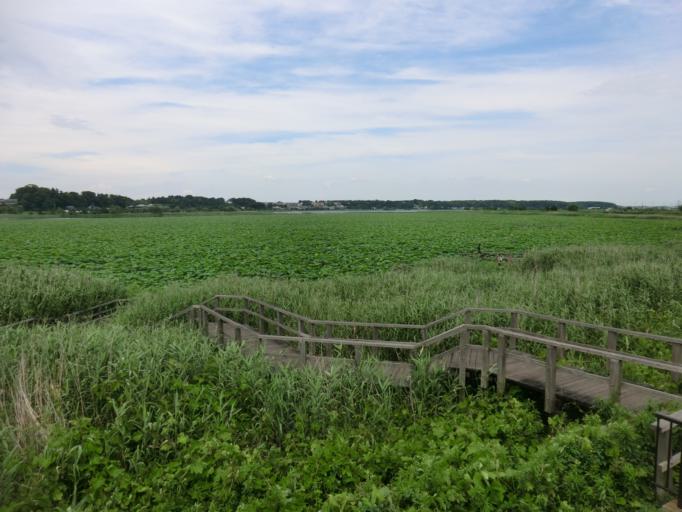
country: JP
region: Chiba
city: Abiko
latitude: 35.8539
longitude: 140.0298
